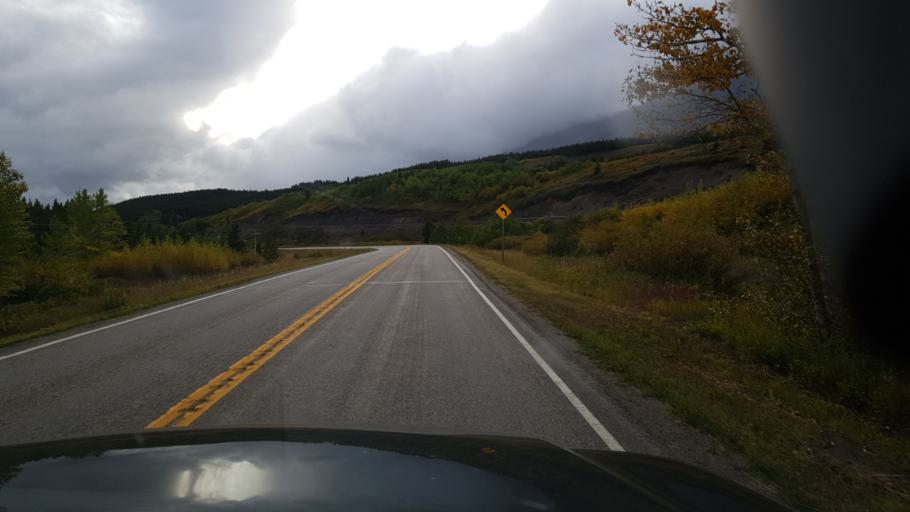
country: US
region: Montana
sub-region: Glacier County
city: South Browning
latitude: 48.3470
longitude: -113.3140
